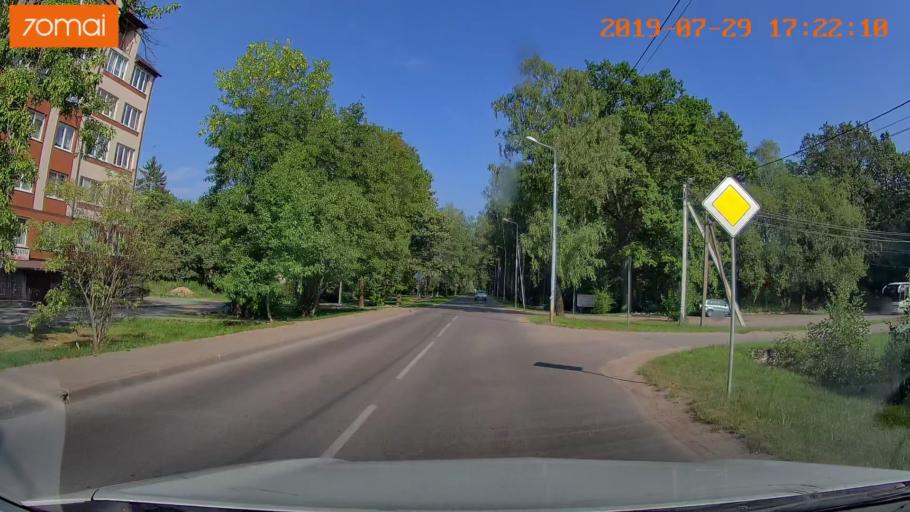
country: RU
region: Kaliningrad
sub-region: Gorod Kaliningrad
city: Kaliningrad
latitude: 54.7695
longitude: 20.4391
